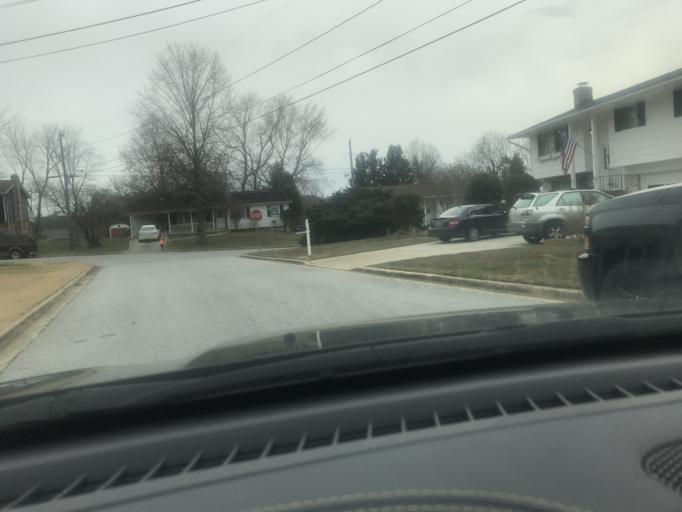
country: US
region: Maryland
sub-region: Prince George's County
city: Oxon Hill
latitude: 38.7968
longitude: -76.9711
